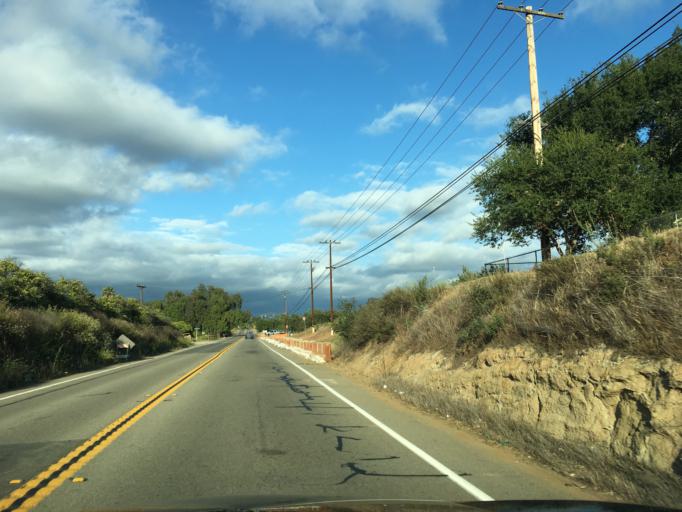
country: US
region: California
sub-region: San Diego County
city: Hidden Meadows
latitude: 33.2563
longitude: -117.0841
